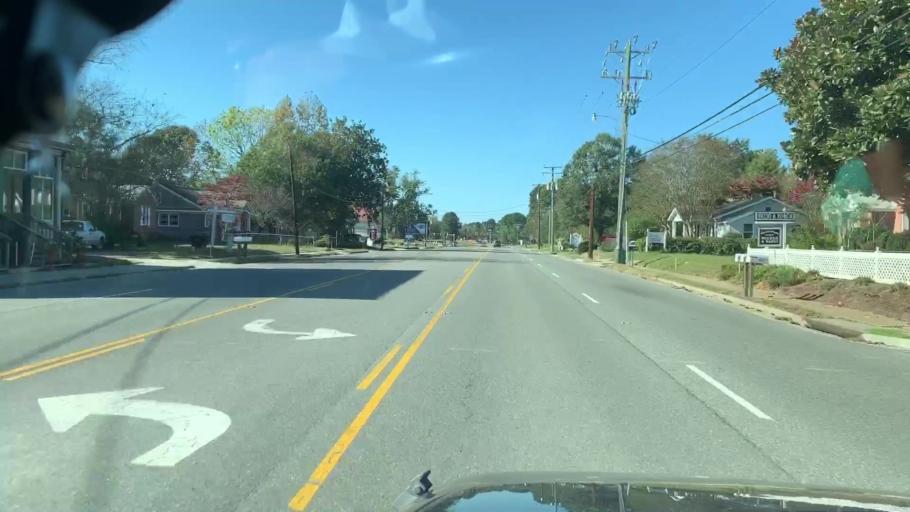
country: US
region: Virginia
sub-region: James City County
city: Williamsburg
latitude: 37.3681
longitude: -76.7707
